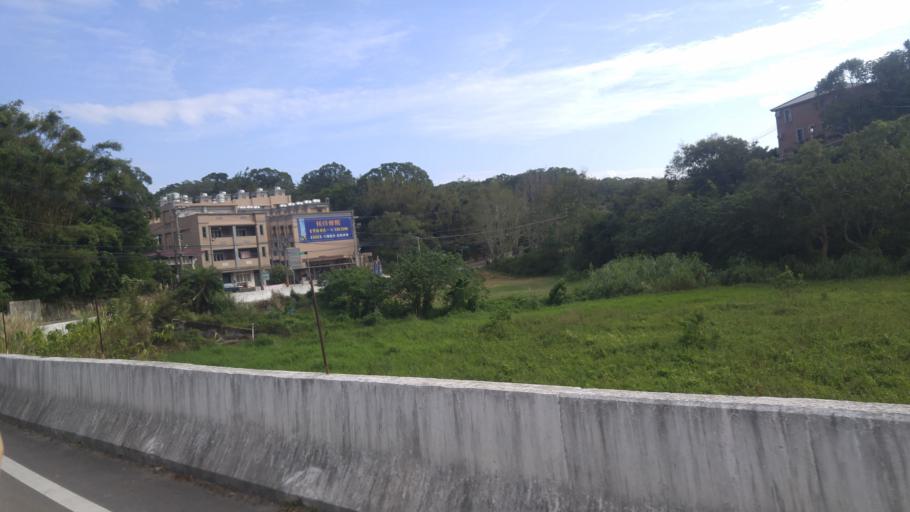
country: TW
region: Taiwan
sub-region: Hsinchu
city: Hsinchu
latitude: 24.7702
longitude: 120.9467
